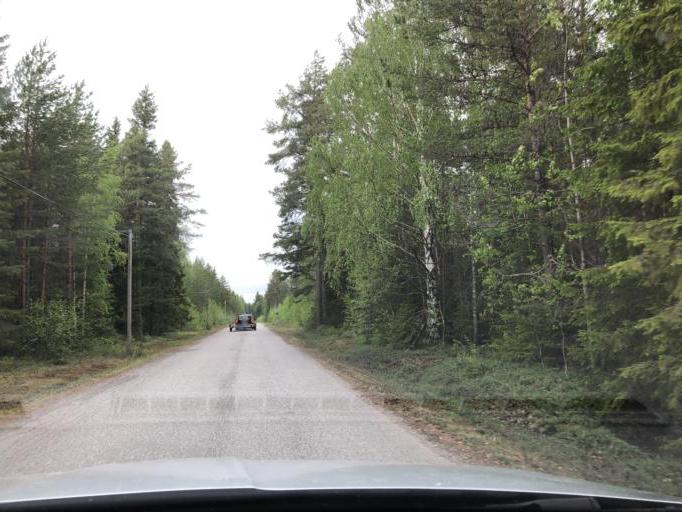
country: SE
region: Norrbotten
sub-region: Pitea Kommun
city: Roknas
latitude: 65.3805
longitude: 21.2739
